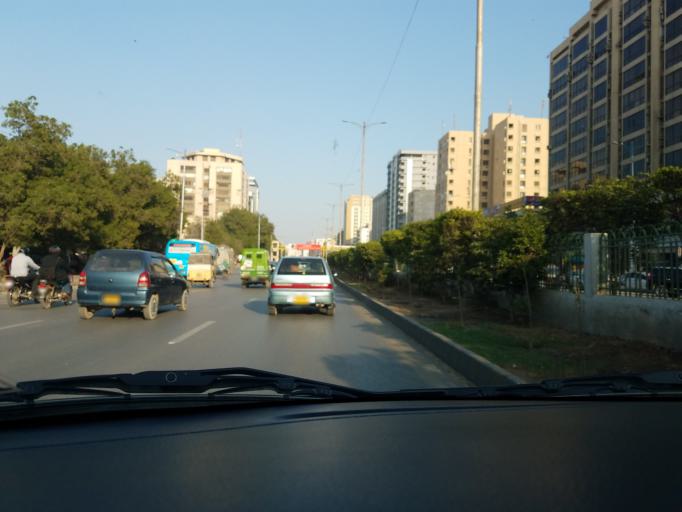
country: PK
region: Sindh
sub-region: Karachi District
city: Karachi
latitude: 24.8604
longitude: 67.0630
